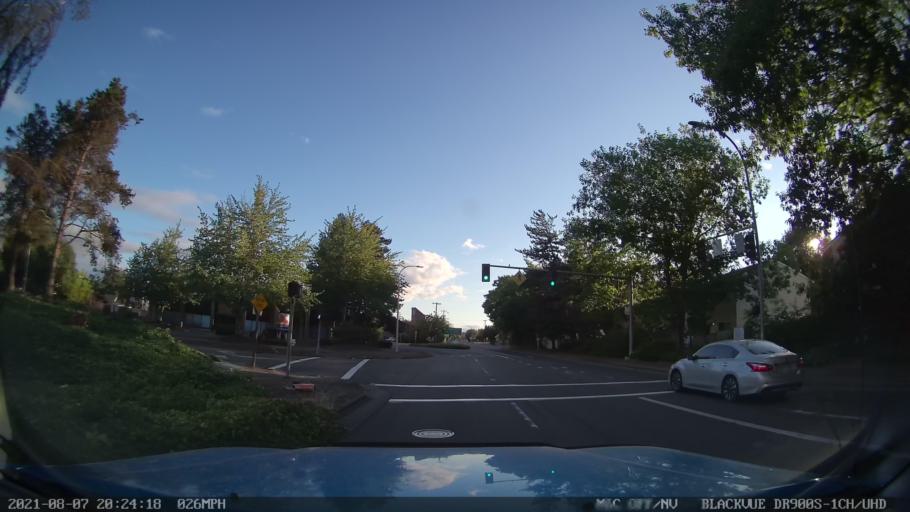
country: US
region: Oregon
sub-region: Marion County
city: Salem
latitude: 44.9560
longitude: -123.0215
